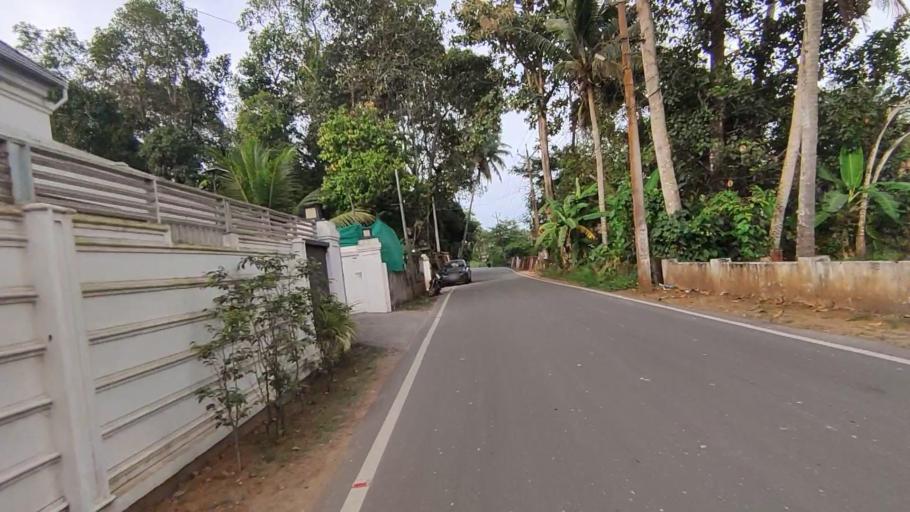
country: IN
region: Kerala
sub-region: Kottayam
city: Kottayam
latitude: 9.5932
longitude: 76.5007
